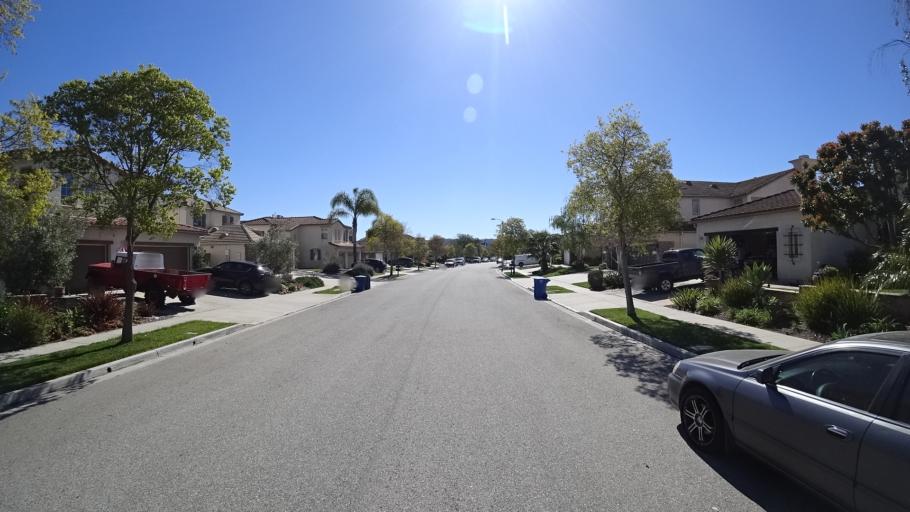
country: US
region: California
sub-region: Ventura County
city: Casa Conejo
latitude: 34.1743
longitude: -118.9804
